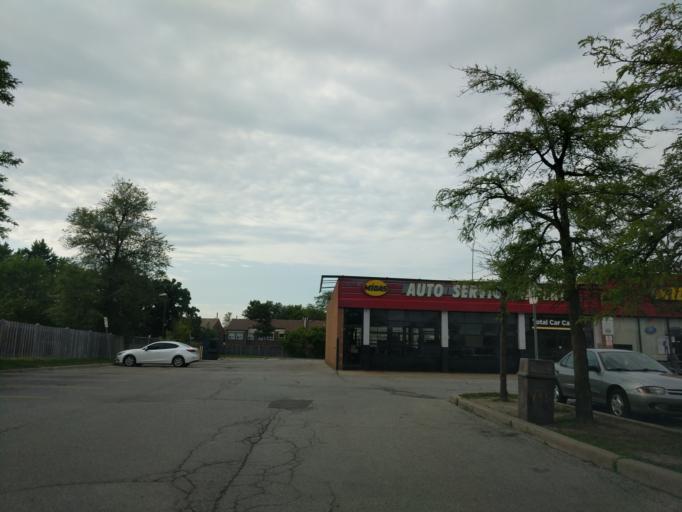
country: CA
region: Ontario
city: Willowdale
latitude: 43.7938
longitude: -79.3305
